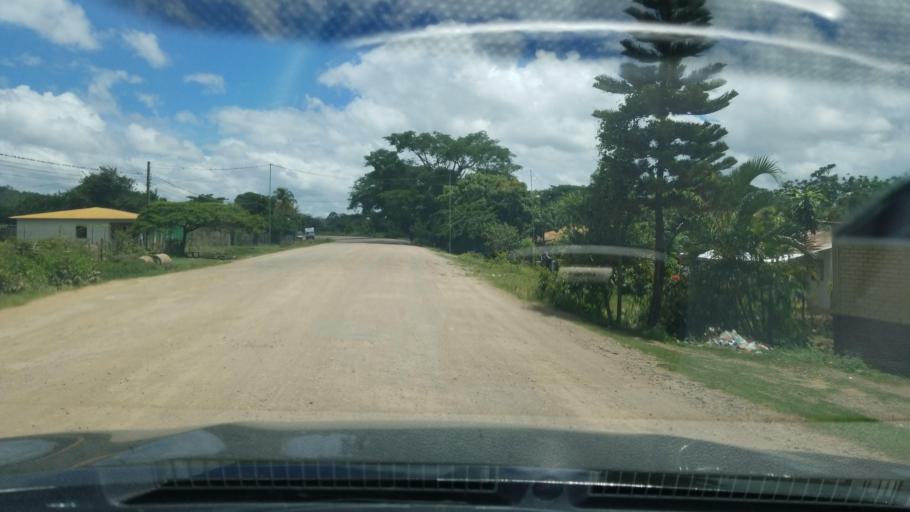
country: HN
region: Francisco Morazan
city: Talanga
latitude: 14.3688
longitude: -87.0548
